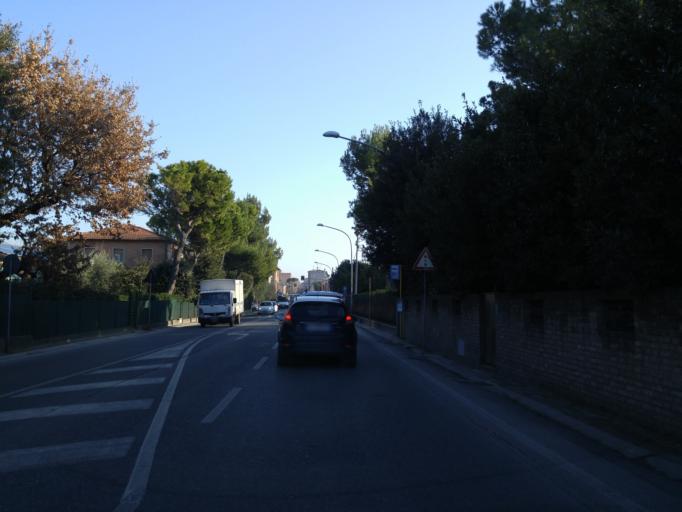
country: IT
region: The Marches
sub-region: Provincia di Pesaro e Urbino
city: Fano
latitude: 43.8497
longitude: 13.0079
